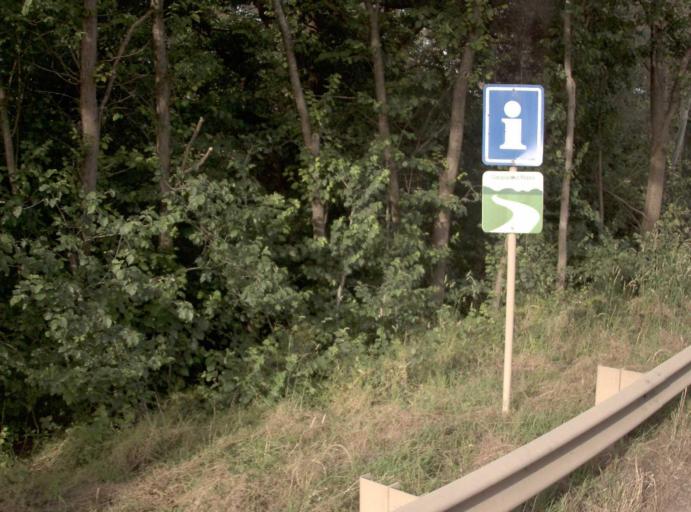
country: AU
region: Victoria
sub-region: Wellington
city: Sale
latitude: -37.9652
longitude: 146.9668
